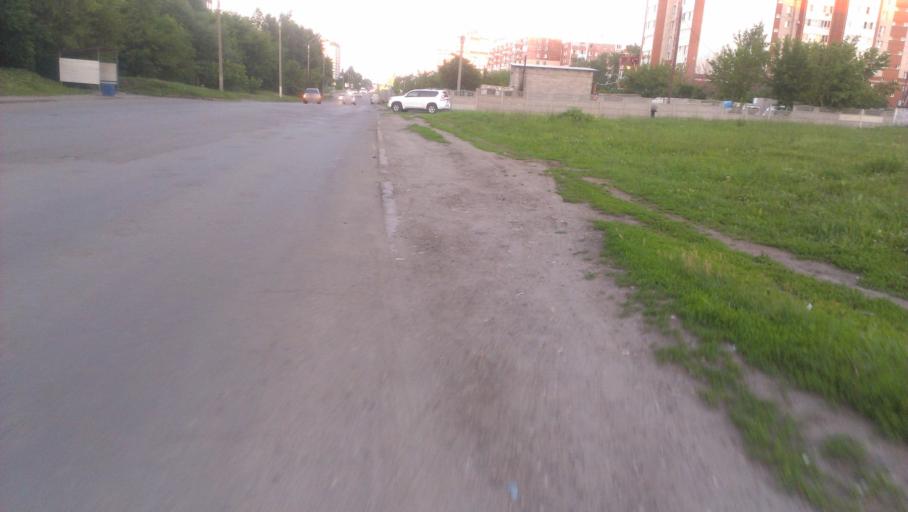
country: RU
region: Altai Krai
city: Novosilikatnyy
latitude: 53.3631
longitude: 83.6641
